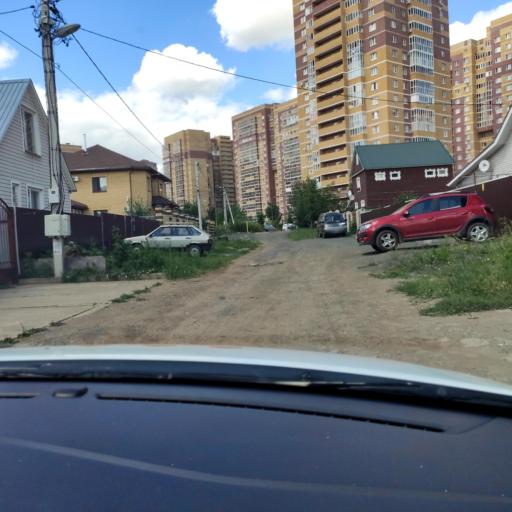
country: RU
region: Tatarstan
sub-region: Gorod Kazan'
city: Kazan
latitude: 55.7789
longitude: 49.2421
